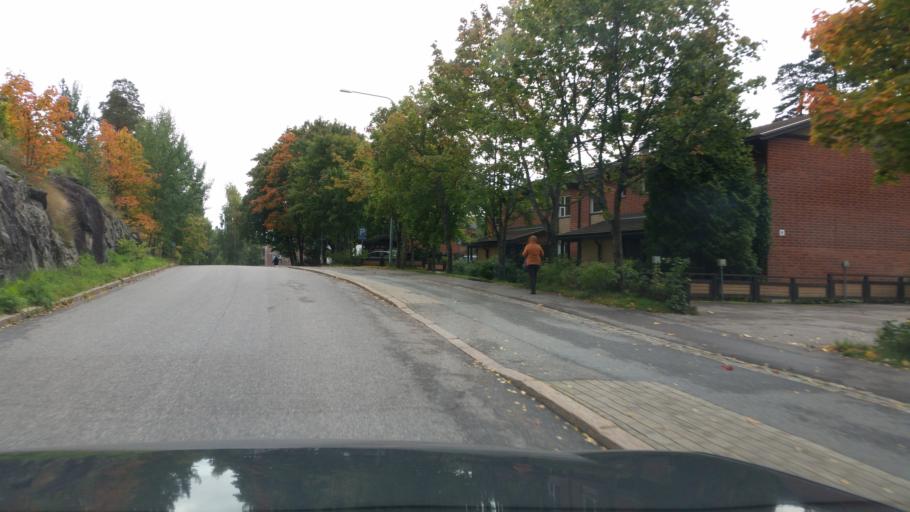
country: FI
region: Uusimaa
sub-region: Helsinki
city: Helsinki
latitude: 60.2350
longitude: 24.9720
